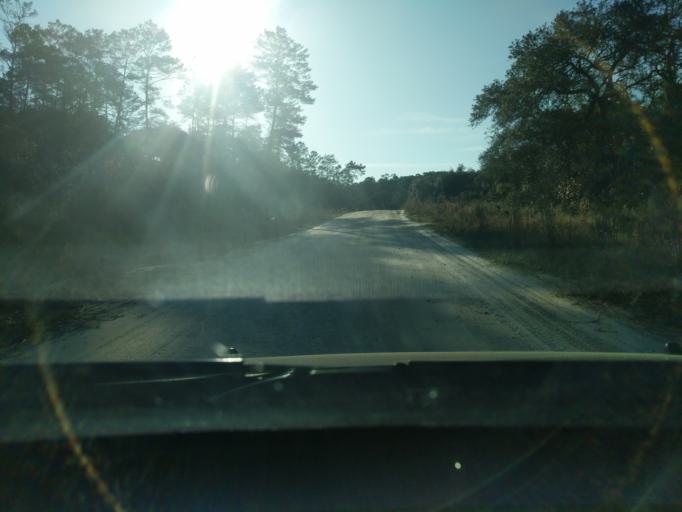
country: US
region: Florida
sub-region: Marion County
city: Silver Springs Shores
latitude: 29.2174
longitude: -81.8248
